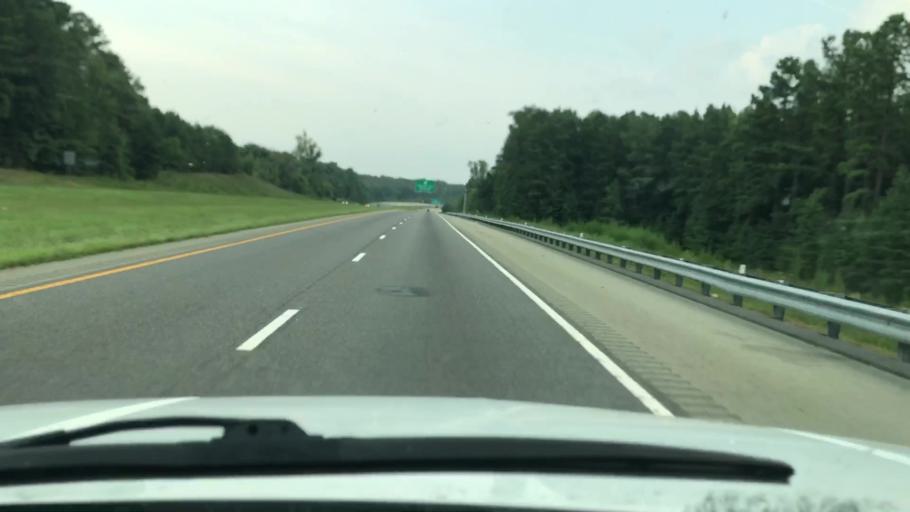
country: US
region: Virginia
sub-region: Chesterfield County
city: Brandermill
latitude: 37.5456
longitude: -77.6938
